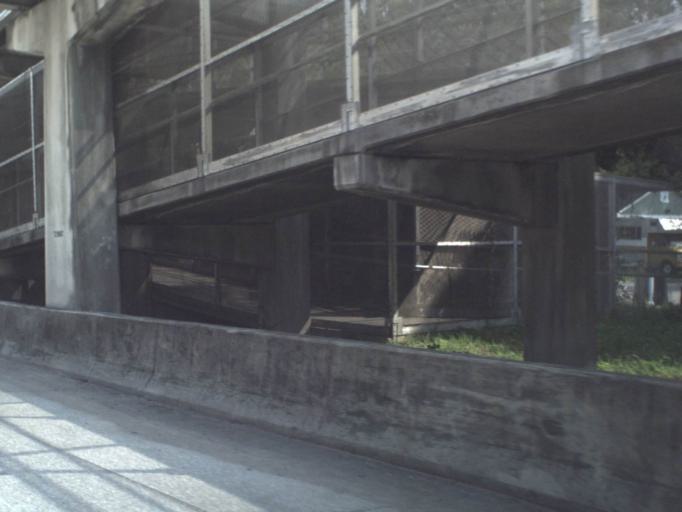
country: US
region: Florida
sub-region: Duval County
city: Jacksonville
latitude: 30.2778
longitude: -81.6180
